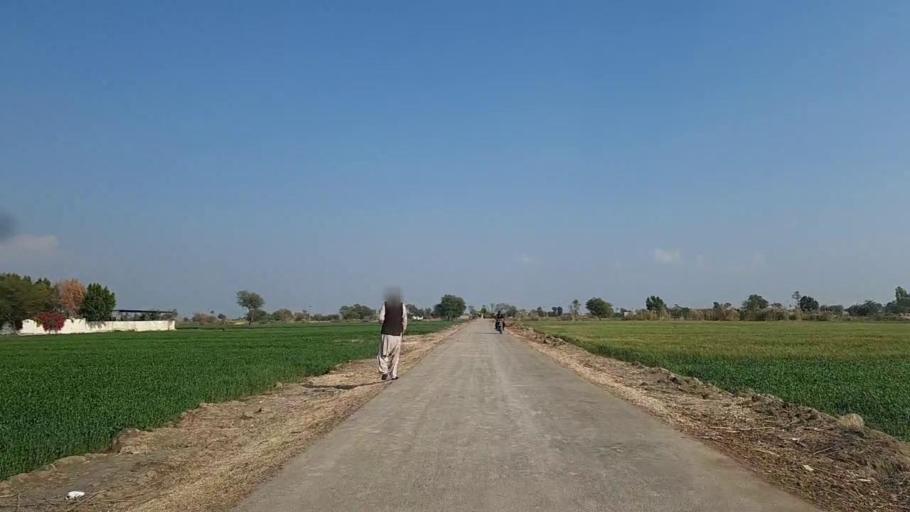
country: PK
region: Sindh
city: Jam Sahib
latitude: 26.2788
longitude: 68.6145
